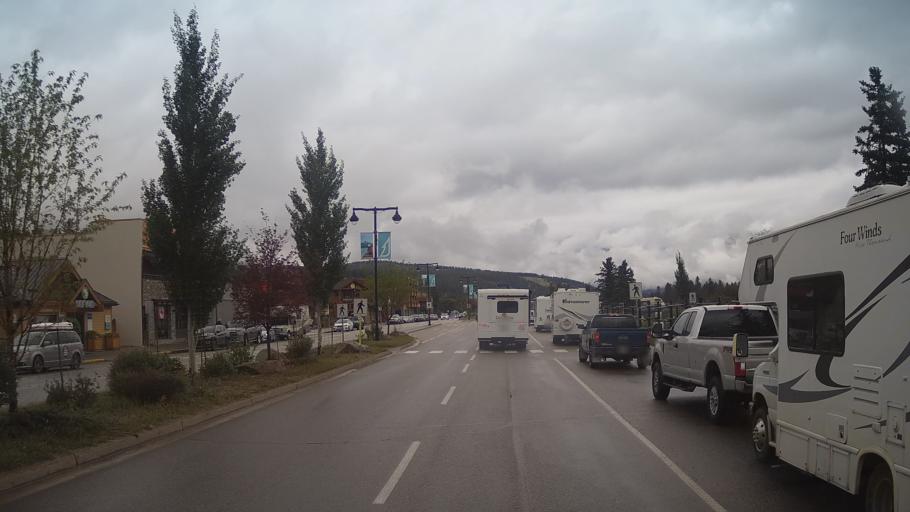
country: CA
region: Alberta
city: Jasper Park Lodge
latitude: 52.8795
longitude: -118.0790
